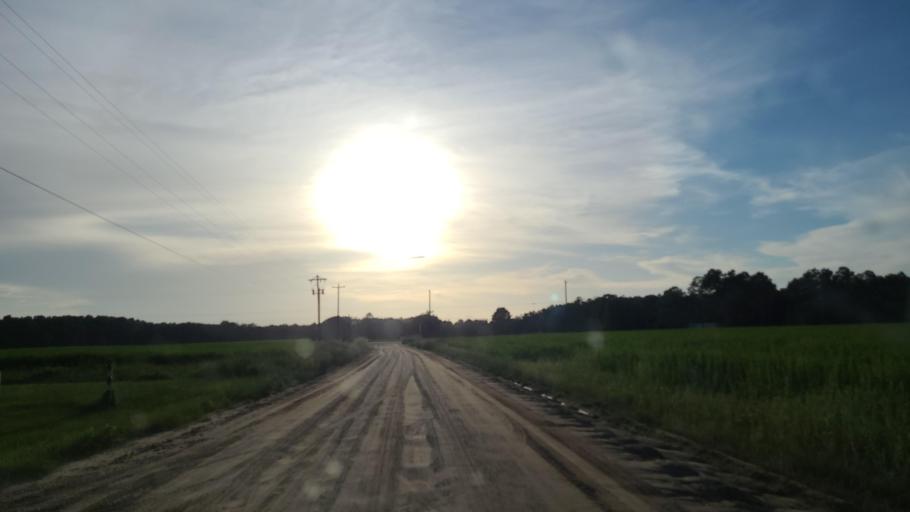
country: US
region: Georgia
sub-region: Echols County
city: Statenville
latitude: 30.6586
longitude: -83.1824
